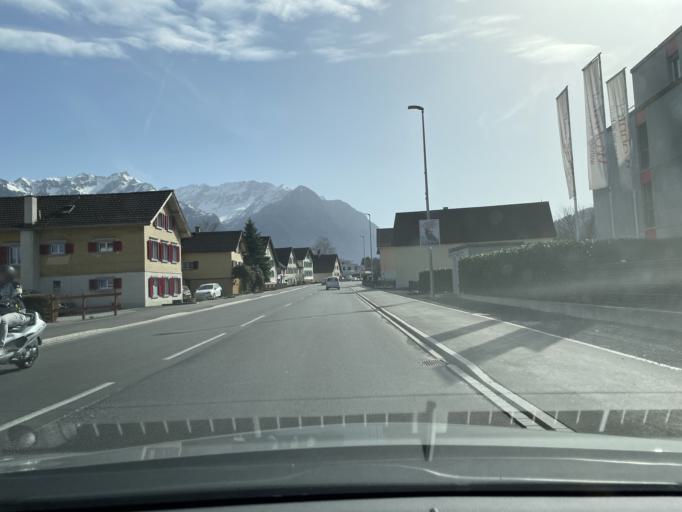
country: CH
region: Saint Gallen
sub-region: Wahlkreis Werdenberg
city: Sevelen
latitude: 47.1252
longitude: 9.4868
